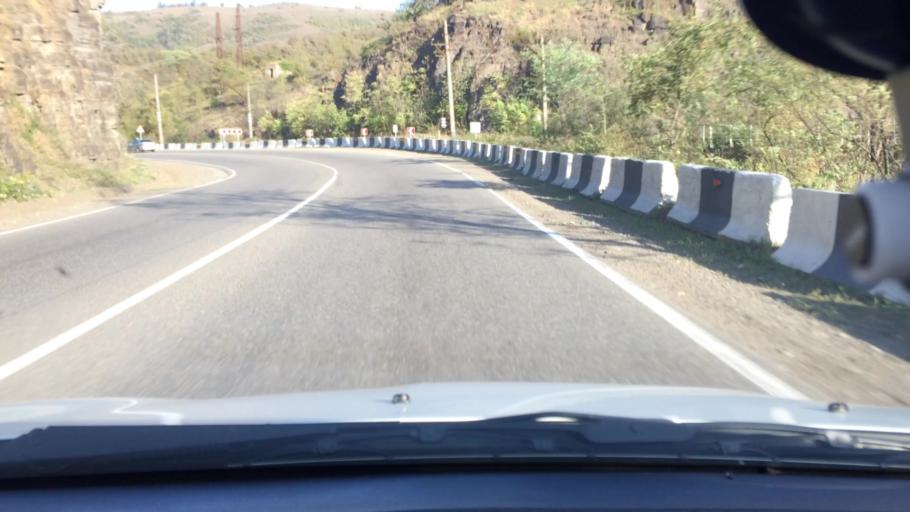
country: GE
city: Shorapani
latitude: 42.0937
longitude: 43.1286
